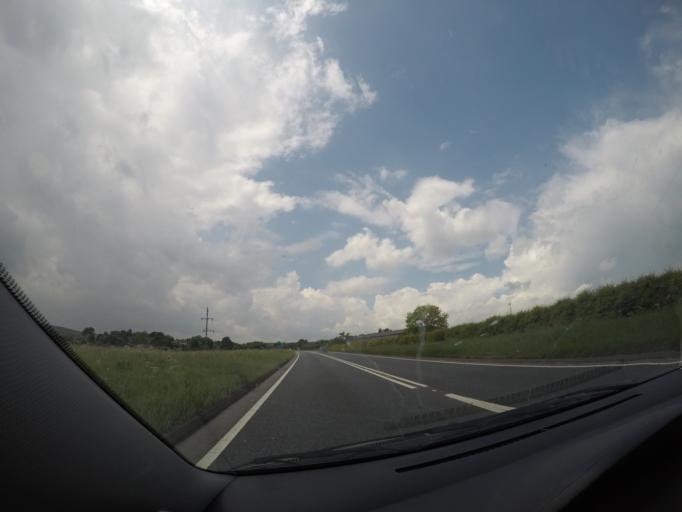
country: GB
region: England
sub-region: County Durham
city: Bowes
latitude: 54.5193
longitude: -2.0041
